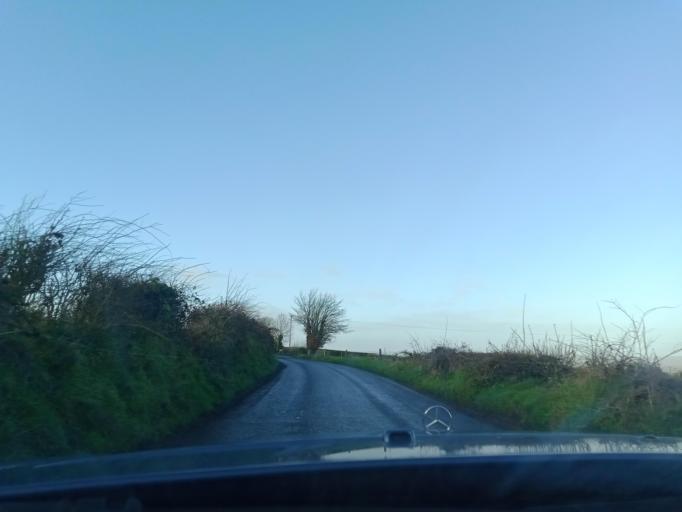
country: IE
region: Leinster
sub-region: Kilkenny
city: Callan
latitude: 52.4746
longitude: -7.4303
